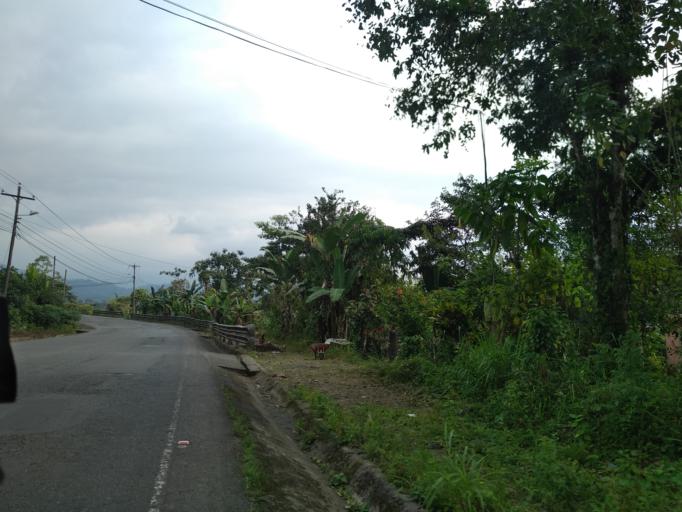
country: EC
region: Cotopaxi
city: La Mana
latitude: -0.9027
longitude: -79.1624
